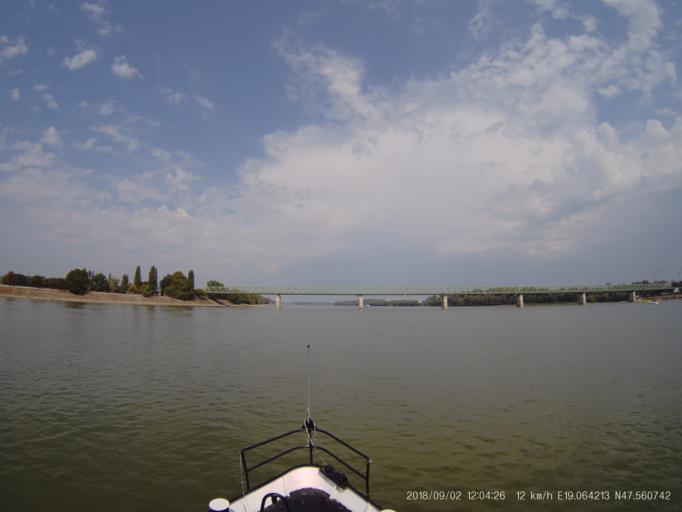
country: HU
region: Budapest
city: Budapest IV. keruelet
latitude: 47.5610
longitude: 19.0637
